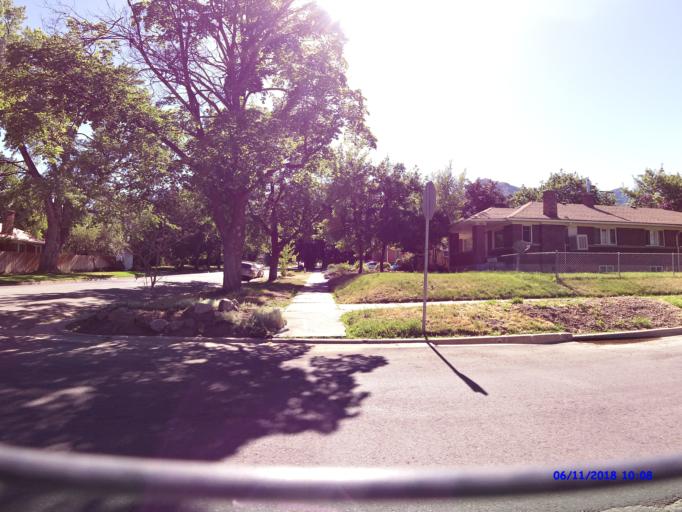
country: US
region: Utah
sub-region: Weber County
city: Ogden
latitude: 41.2181
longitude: -111.9456
